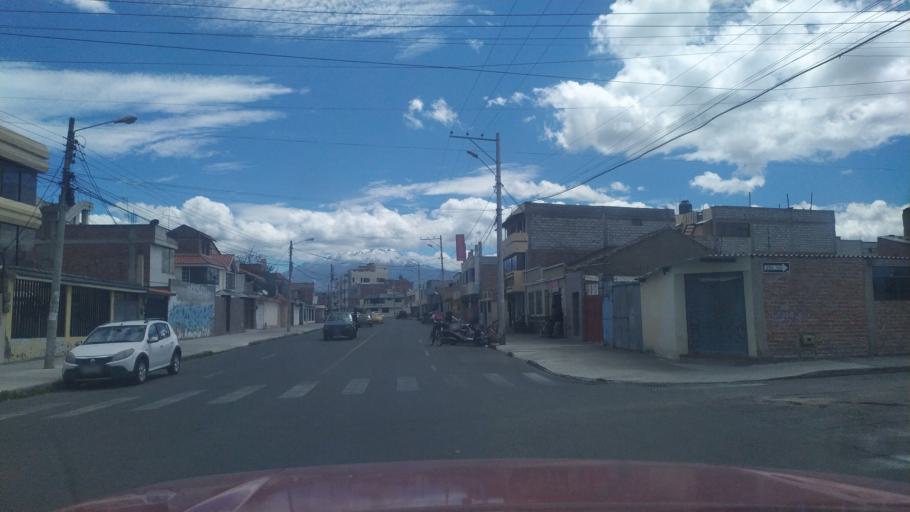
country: EC
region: Chimborazo
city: Riobamba
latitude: -1.6808
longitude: -78.6457
